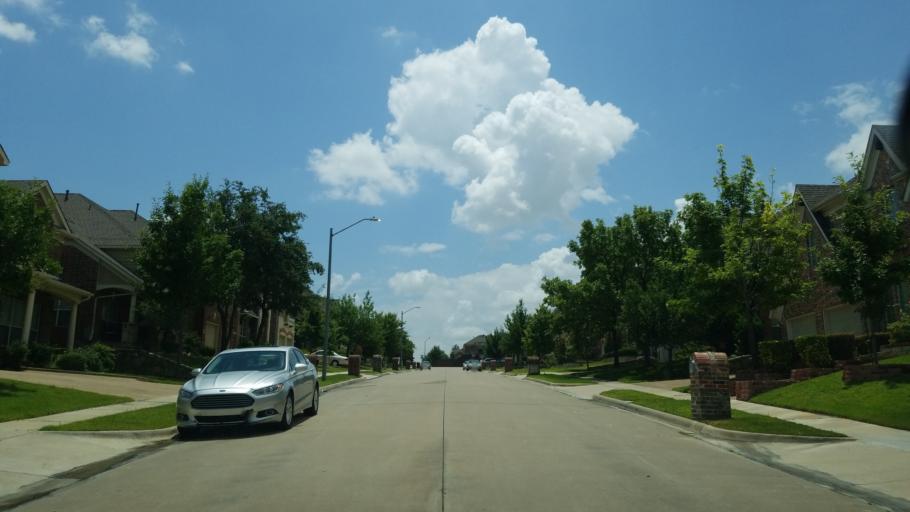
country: US
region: Texas
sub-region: Dallas County
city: Coppell
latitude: 32.9461
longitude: -96.9663
